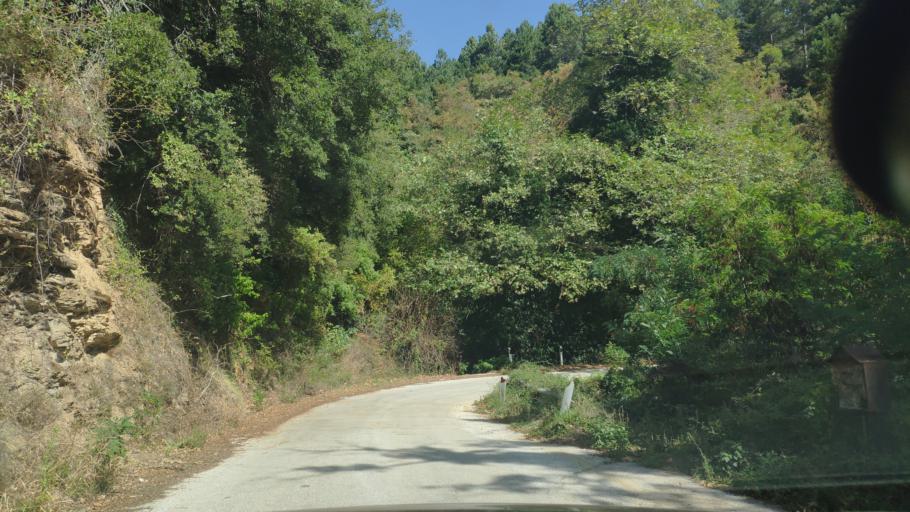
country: GR
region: Peloponnese
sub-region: Nomos Korinthias
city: Nemea
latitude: 37.8658
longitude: 22.3851
